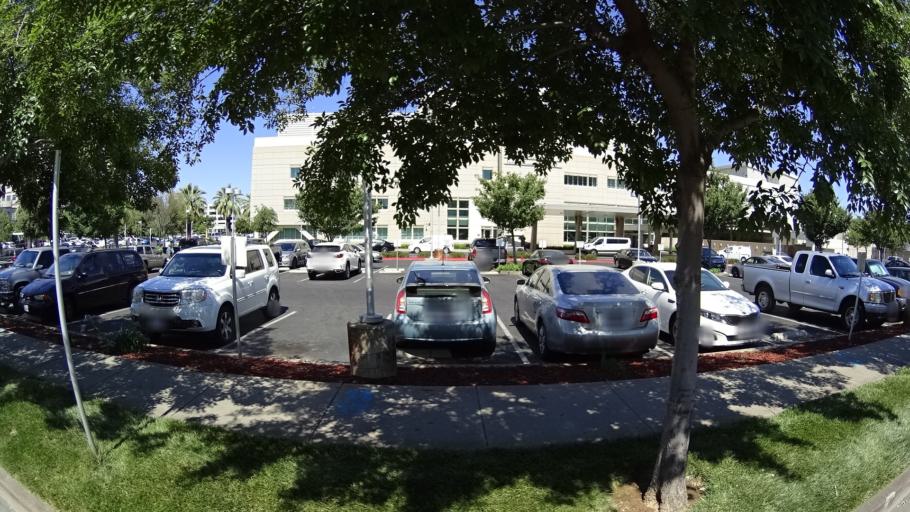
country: US
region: California
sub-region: Sacramento County
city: Sacramento
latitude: 38.5543
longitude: -121.4532
